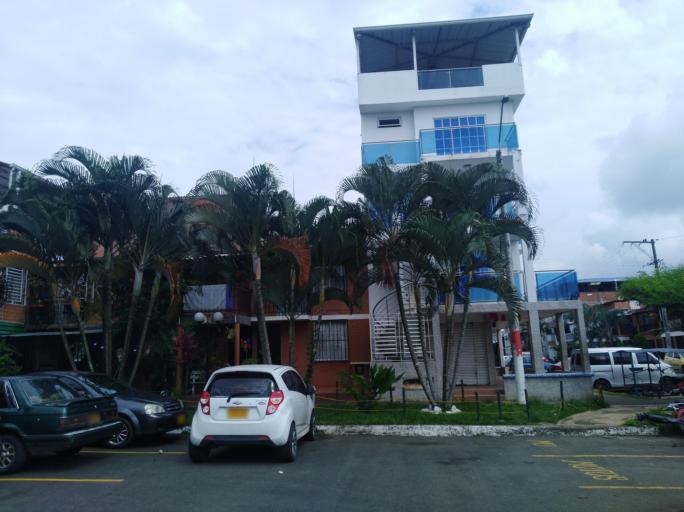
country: CO
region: Valle del Cauca
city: Cali
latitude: 3.3938
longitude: -76.5111
